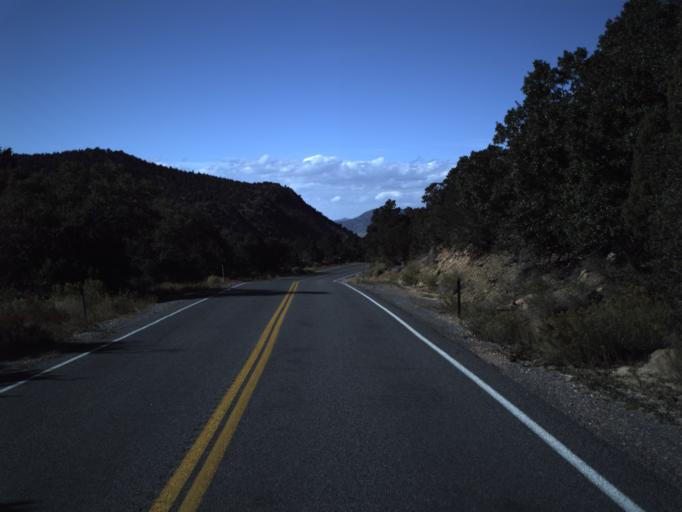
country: US
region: Utah
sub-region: Iron County
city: Parowan
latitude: 37.8210
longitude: -112.8102
